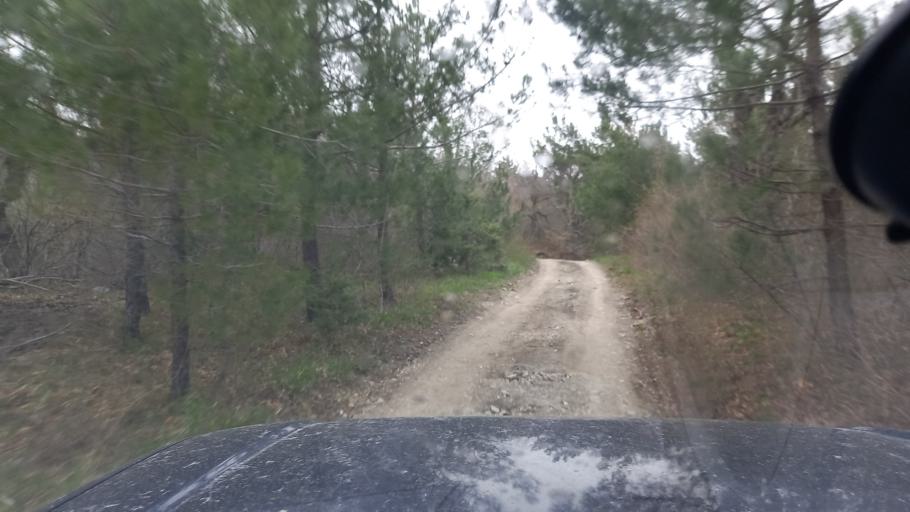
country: RU
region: Krasnodarskiy
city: Dzhubga
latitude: 44.3194
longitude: 38.6788
